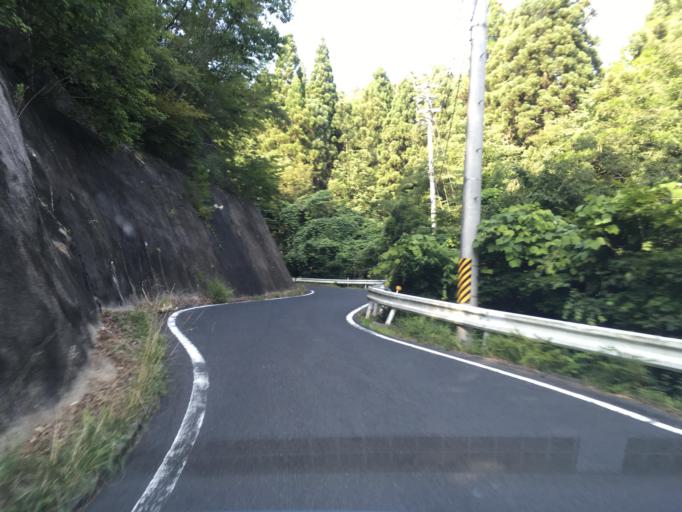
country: JP
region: Iwate
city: Ofunato
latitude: 38.9156
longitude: 141.6038
